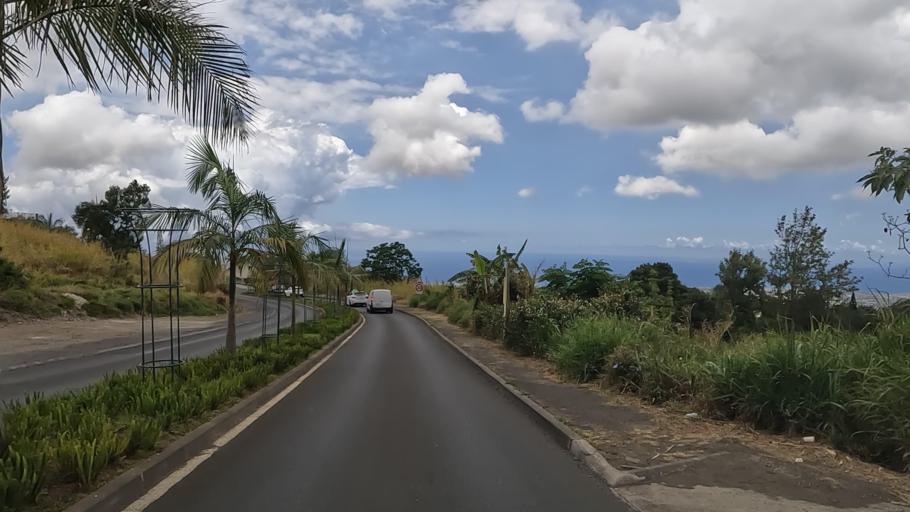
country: RE
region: Reunion
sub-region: Reunion
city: Le Tampon
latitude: -21.2651
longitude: 55.5126
